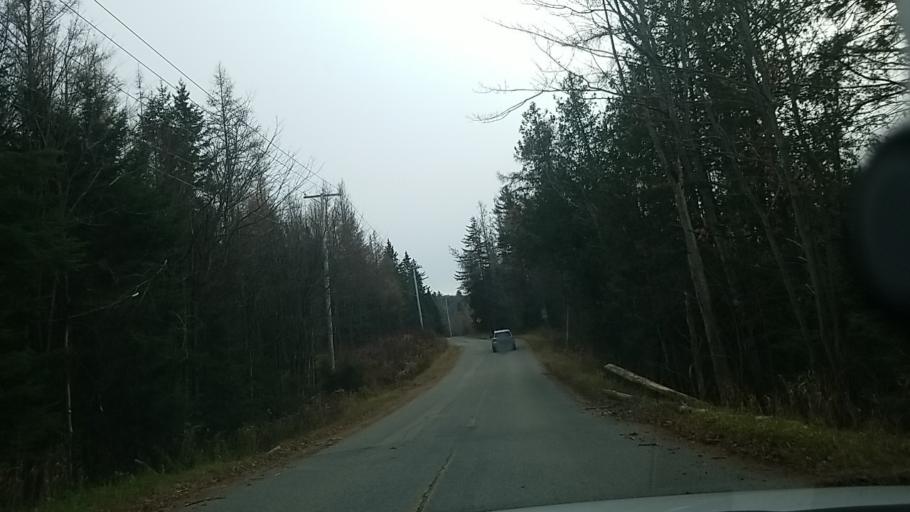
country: CA
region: Quebec
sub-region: Laurentides
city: Saint-Sauveur
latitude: 45.8192
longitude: -74.2488
